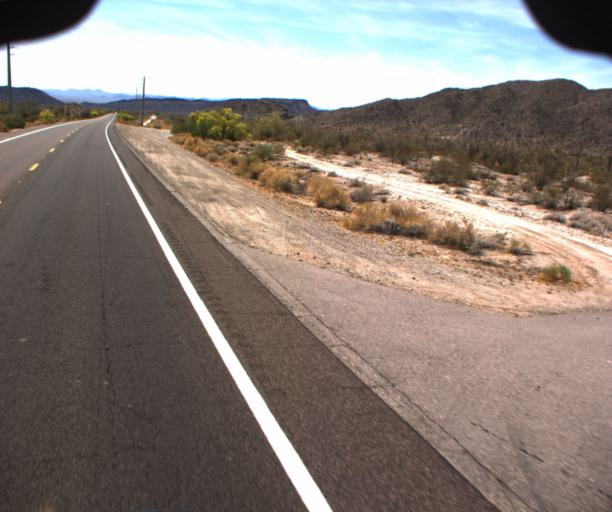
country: US
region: Arizona
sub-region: La Paz County
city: Salome
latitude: 33.7377
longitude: -113.6764
